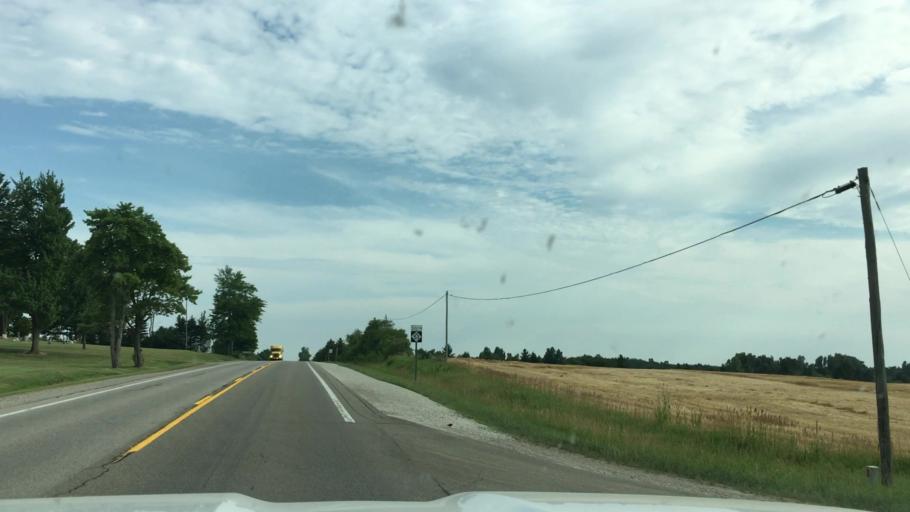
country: US
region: Michigan
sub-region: Sanilac County
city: Brown City
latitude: 43.1889
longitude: -83.0766
